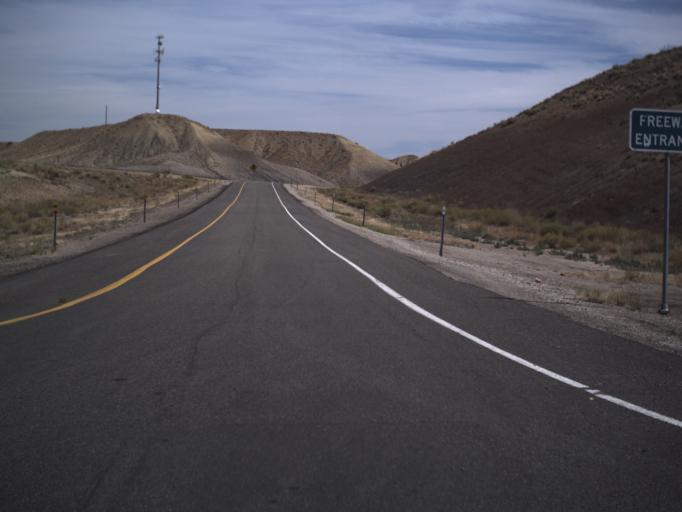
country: US
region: Utah
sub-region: Grand County
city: Moab
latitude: 38.9611
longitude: -109.7220
